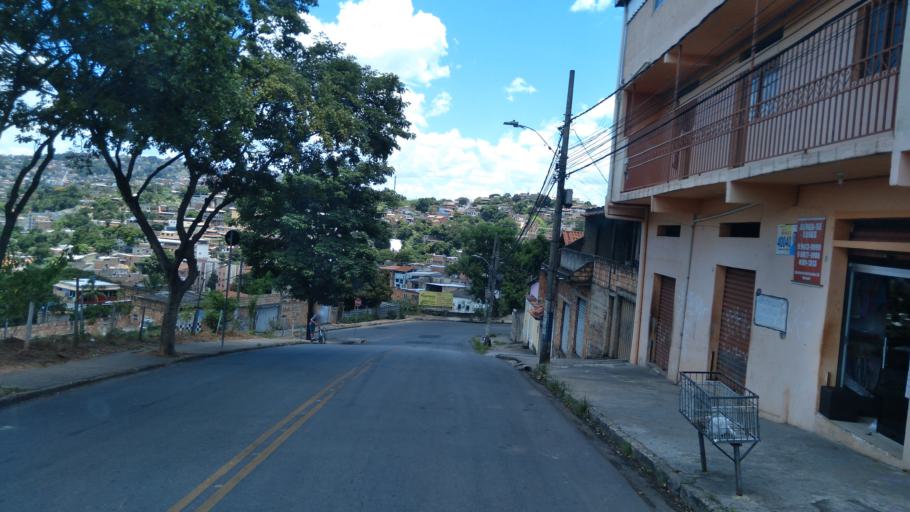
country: BR
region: Minas Gerais
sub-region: Santa Luzia
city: Santa Luzia
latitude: -19.8438
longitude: -43.8966
